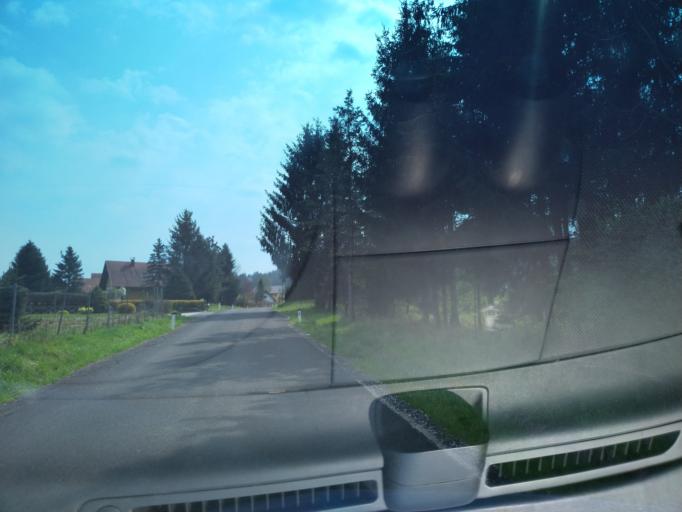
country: AT
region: Styria
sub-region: Politischer Bezirk Leibnitz
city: Kitzeck im Sausal
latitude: 46.7520
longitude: 15.4186
